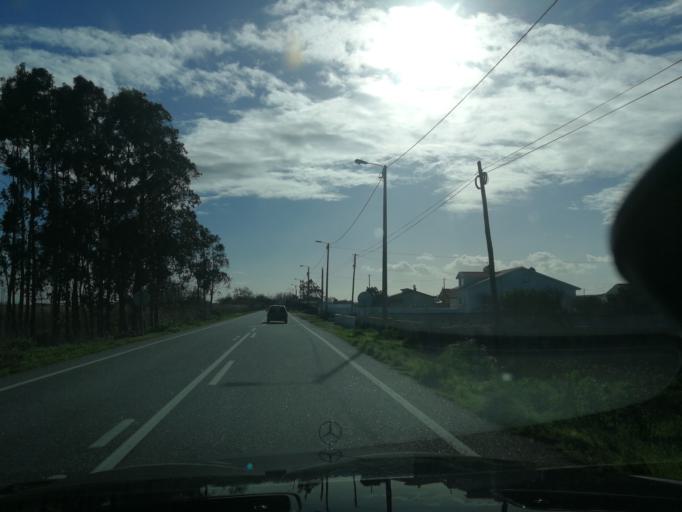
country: PT
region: Aveiro
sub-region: Estarreja
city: Pardilho
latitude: 40.8044
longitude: -8.6729
